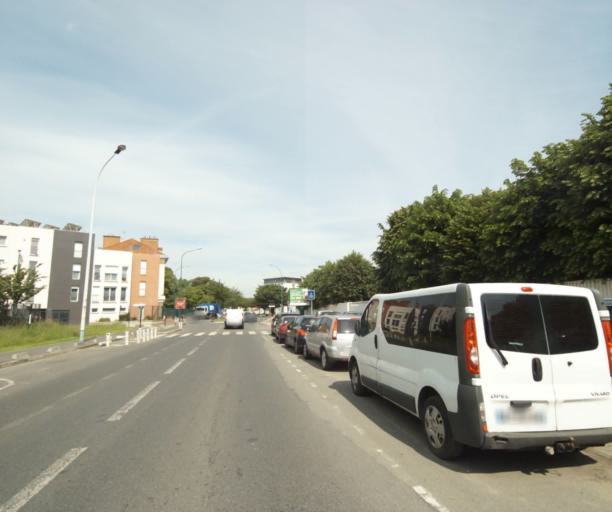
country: FR
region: Ile-de-France
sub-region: Departement des Hauts-de-Seine
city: Gennevilliers
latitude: 48.9312
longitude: 2.3063
